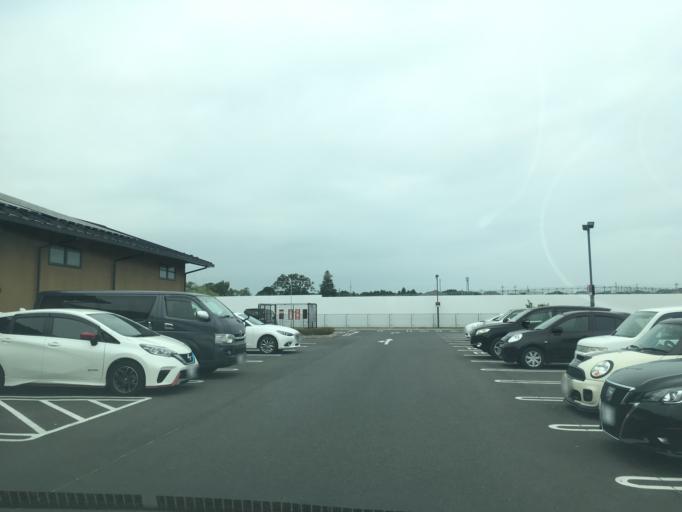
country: JP
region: Ibaraki
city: Hitachi-Naka
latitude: 36.3943
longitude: 140.5016
